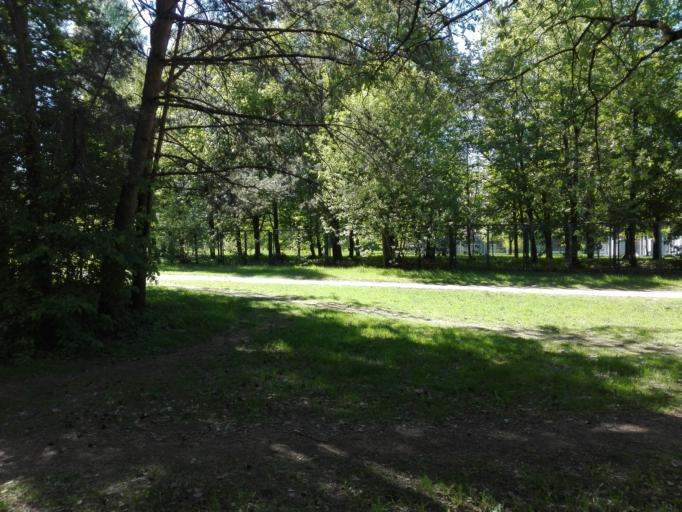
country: LT
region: Vilnius County
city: Lazdynai
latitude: 54.6864
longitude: 25.2164
